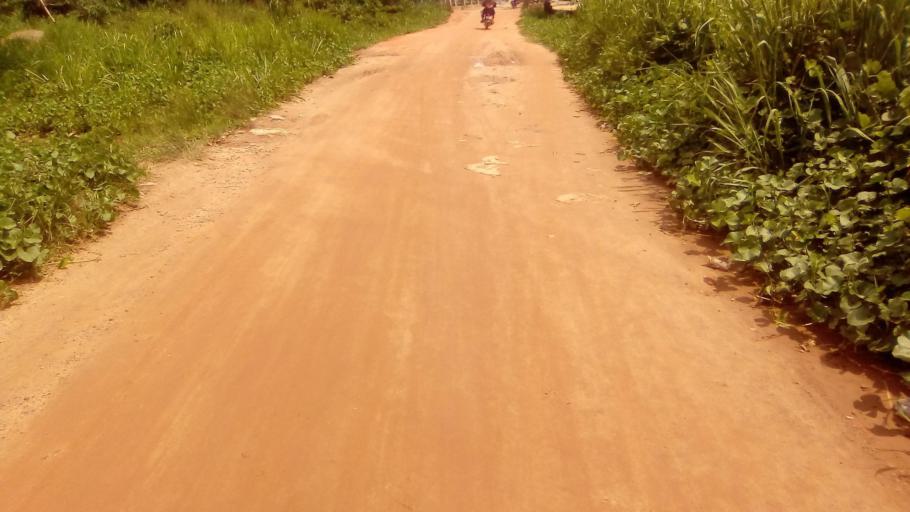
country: SL
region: Southern Province
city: Bo
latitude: 7.9768
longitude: -11.7674
